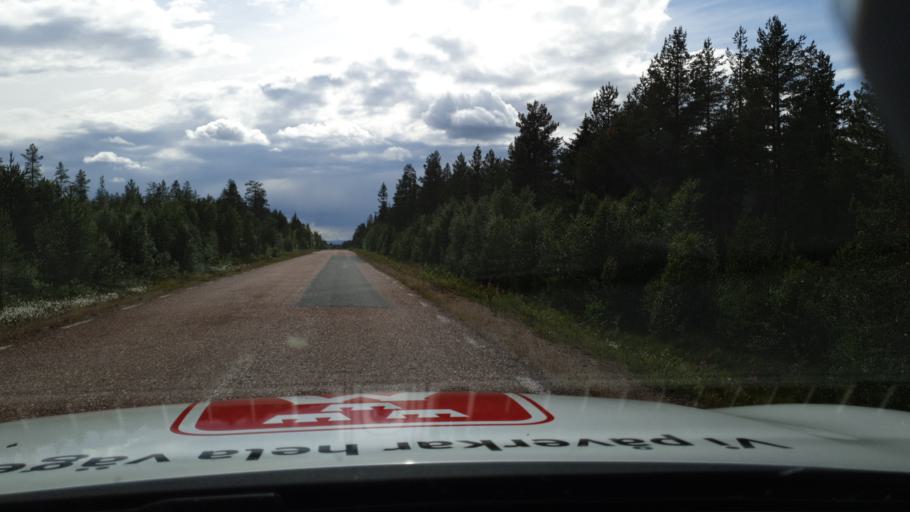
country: SE
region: Dalarna
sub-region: Alvdalens Kommun
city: AElvdalen
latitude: 61.7652
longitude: 13.4728
